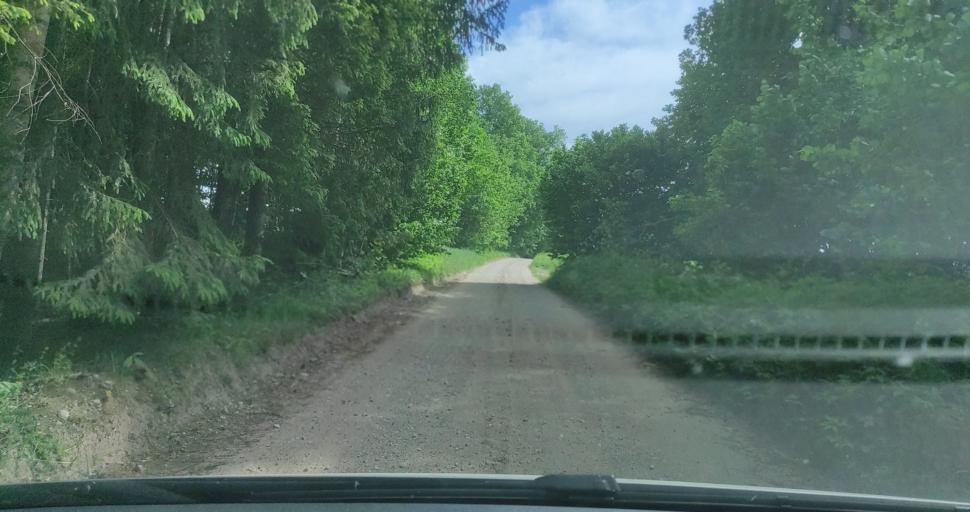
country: LV
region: Kuldigas Rajons
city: Kuldiga
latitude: 56.8628
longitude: 21.9079
